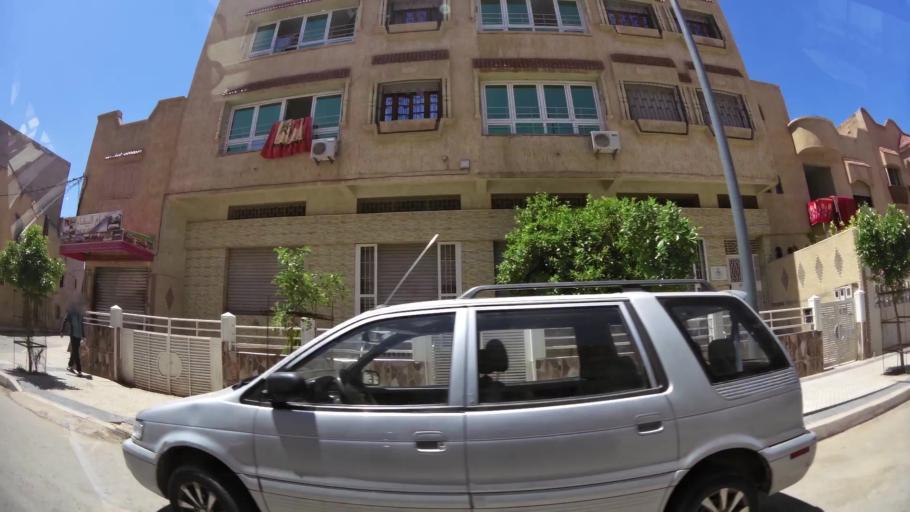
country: MA
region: Oriental
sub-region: Oujda-Angad
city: Oujda
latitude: 34.6625
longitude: -1.9195
